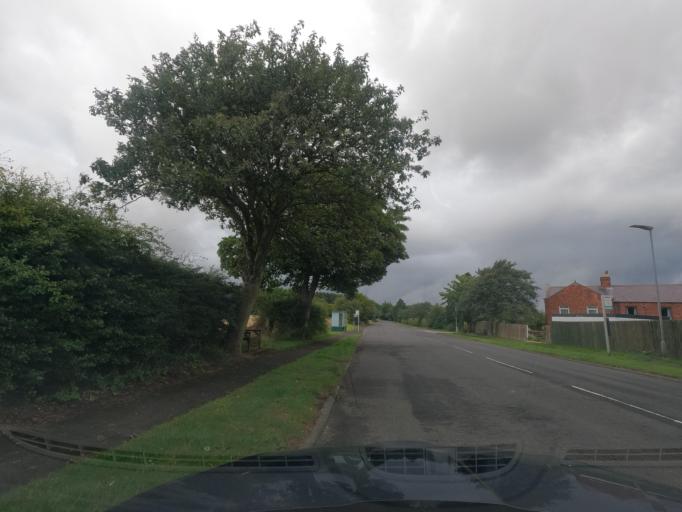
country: GB
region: England
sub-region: Northumberland
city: Ancroft
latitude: 55.7390
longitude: -1.9930
